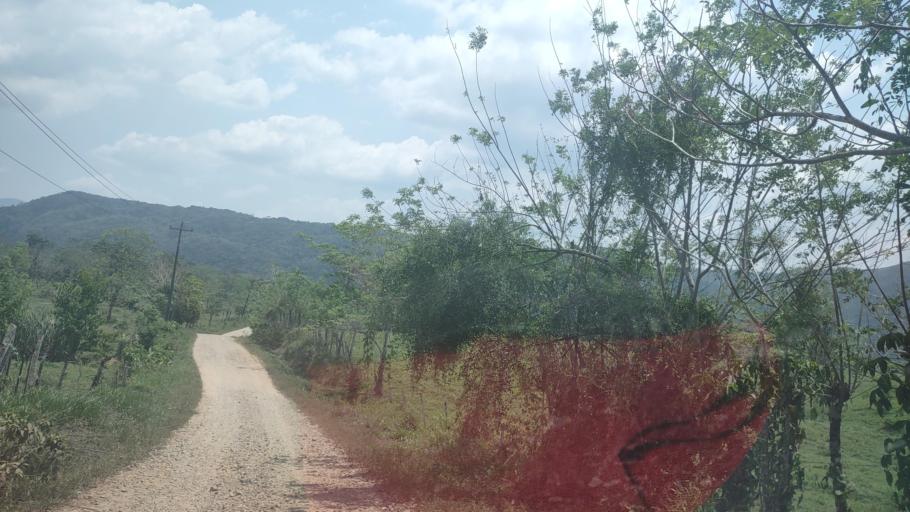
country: MX
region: Chiapas
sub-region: Tecpatan
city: Raudales Malpaso
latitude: 17.2801
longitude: -93.8699
